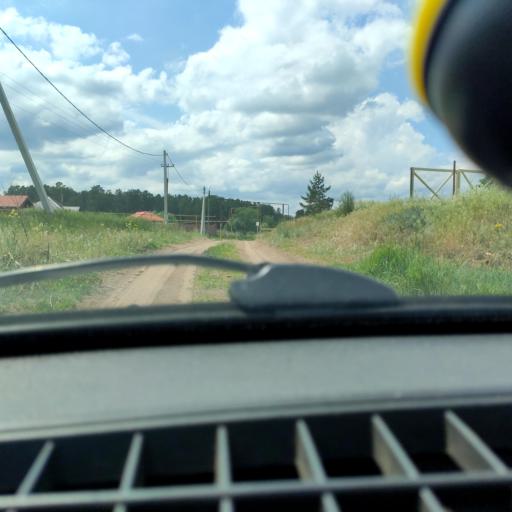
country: RU
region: Samara
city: Povolzhskiy
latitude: 53.6324
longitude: 49.6766
